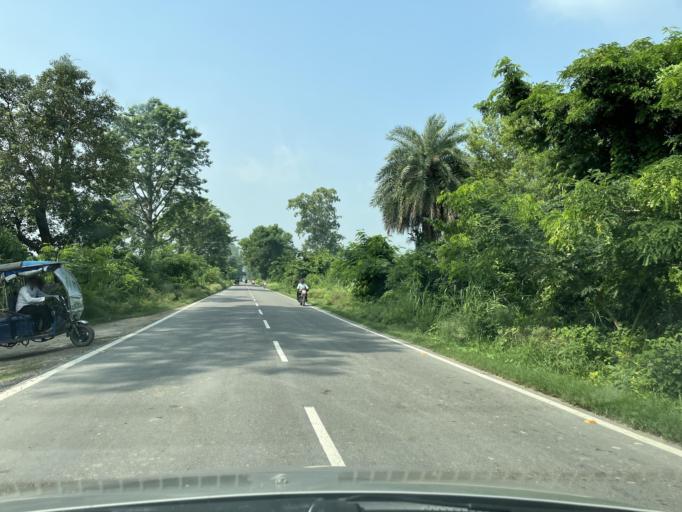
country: IN
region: Uttarakhand
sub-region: Udham Singh Nagar
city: Bazpur
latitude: 29.1804
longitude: 79.1781
